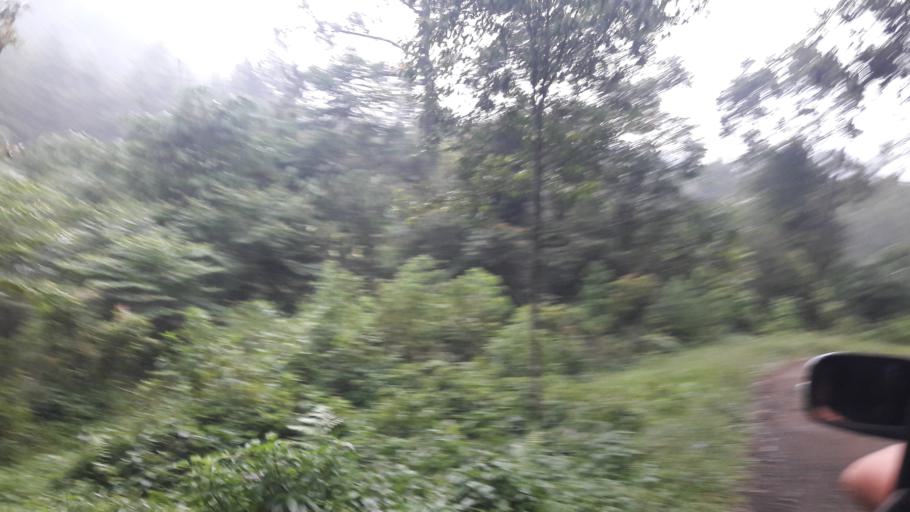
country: ID
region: West Java
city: Cipeundeuy
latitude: -6.6754
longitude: 106.5162
